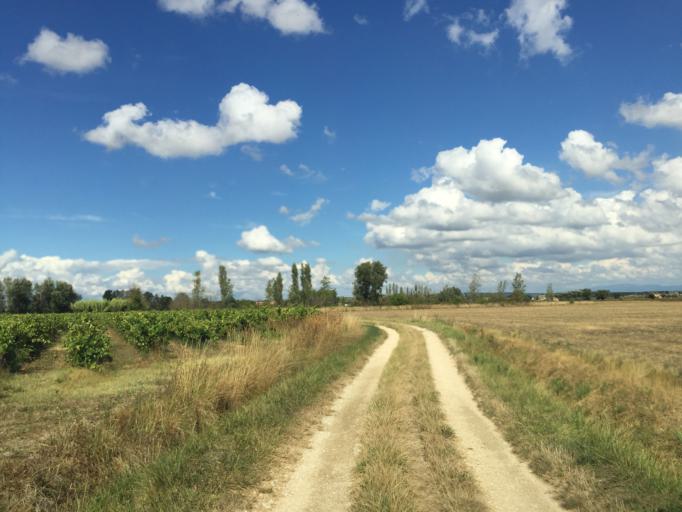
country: FR
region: Provence-Alpes-Cote d'Azur
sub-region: Departement du Vaucluse
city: Caderousse
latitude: 44.1193
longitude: 4.7545
